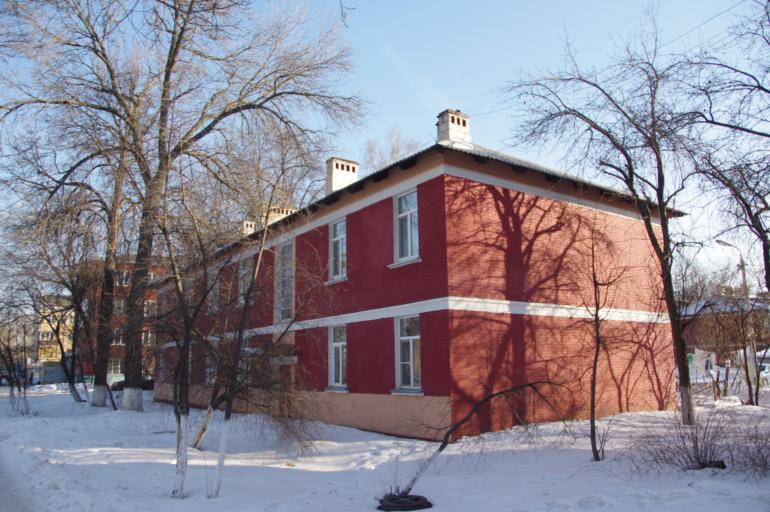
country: RU
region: Moskovskaya
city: Kolomna
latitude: 55.0927
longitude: 38.7723
